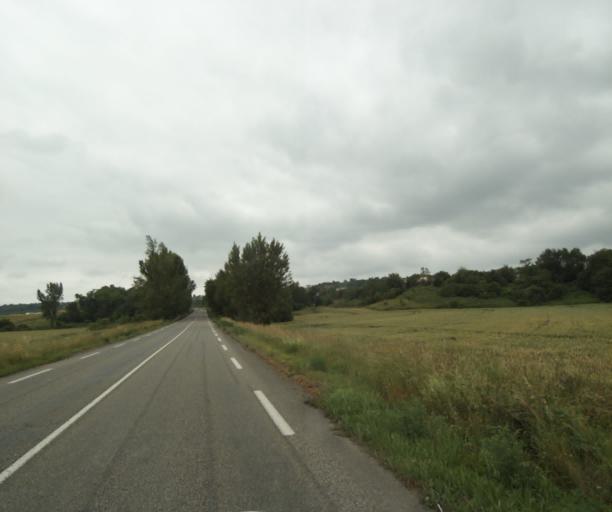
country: FR
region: Midi-Pyrenees
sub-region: Departement du Tarn-et-Garonne
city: Saint-Nauphary
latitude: 43.9863
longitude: 1.3934
